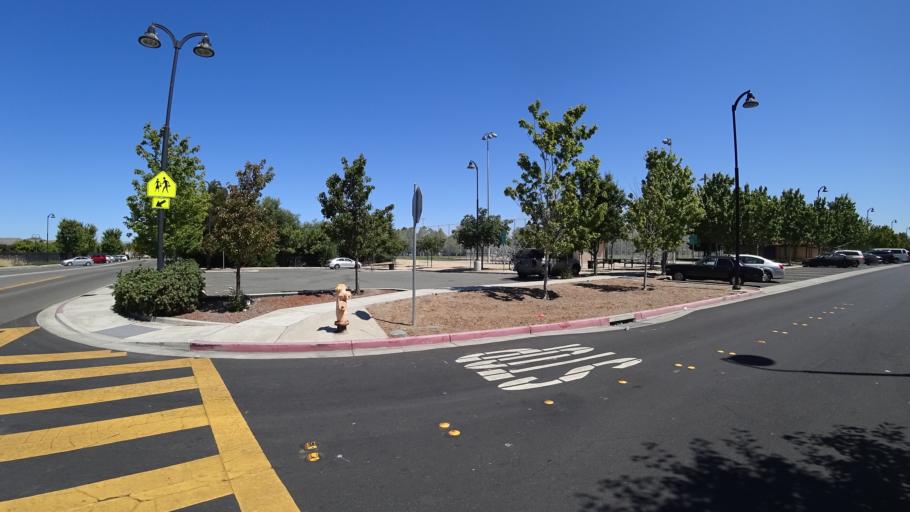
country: US
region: California
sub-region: Alameda County
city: Cherryland
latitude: 37.6646
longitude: -122.0975
